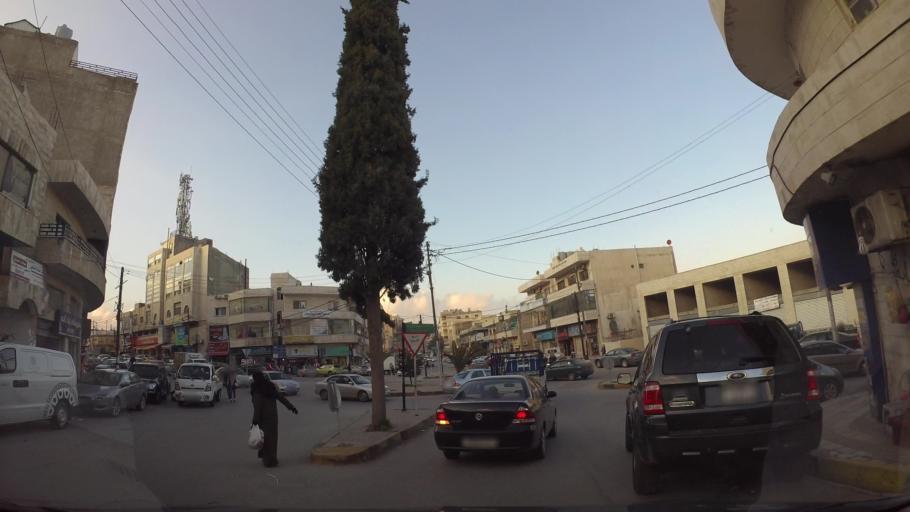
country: JO
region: Amman
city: Amman
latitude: 32.0014
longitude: 35.9419
